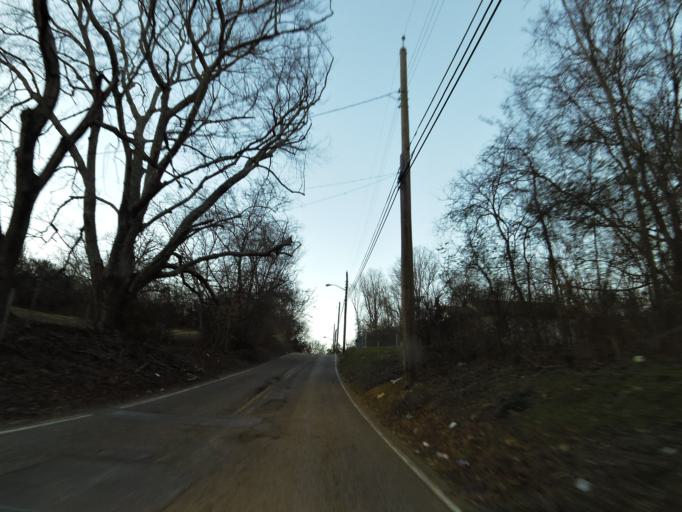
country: US
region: Tennessee
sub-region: Knox County
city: Knoxville
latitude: 35.9855
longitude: -83.9627
